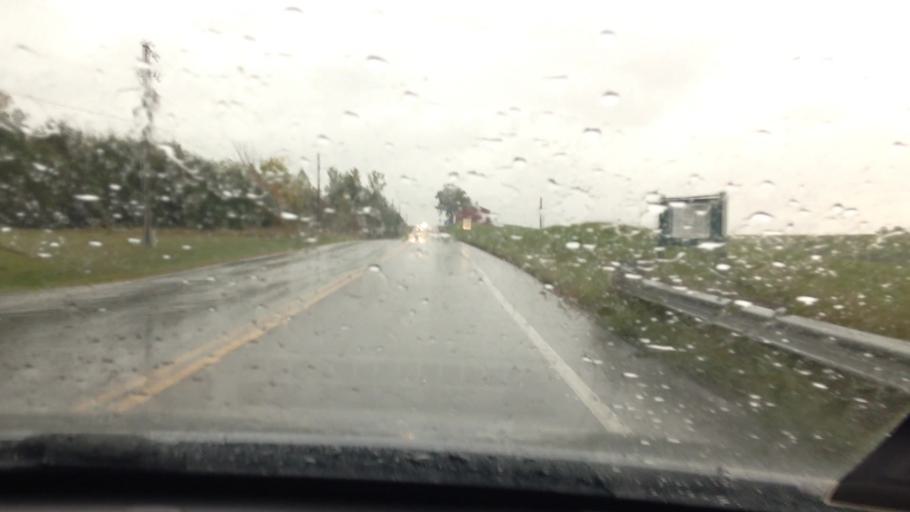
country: US
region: Missouri
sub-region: Platte County
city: Weston
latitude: 39.3928
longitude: -94.8634
